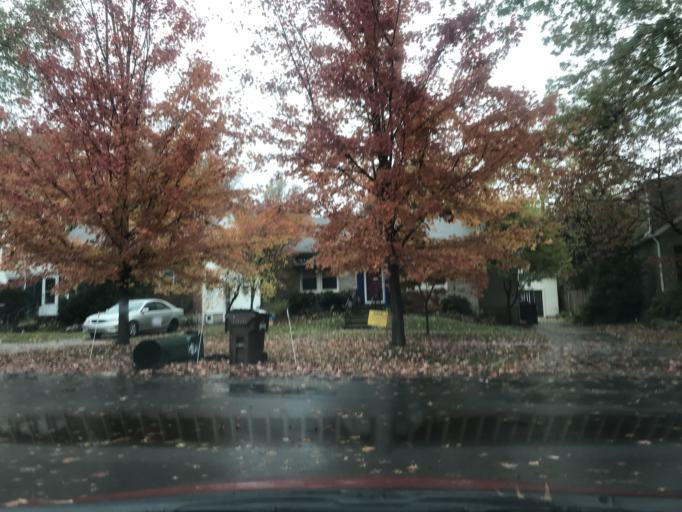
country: US
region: Kentucky
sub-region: Jefferson County
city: Saint Matthews
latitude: 38.2491
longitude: -85.6487
